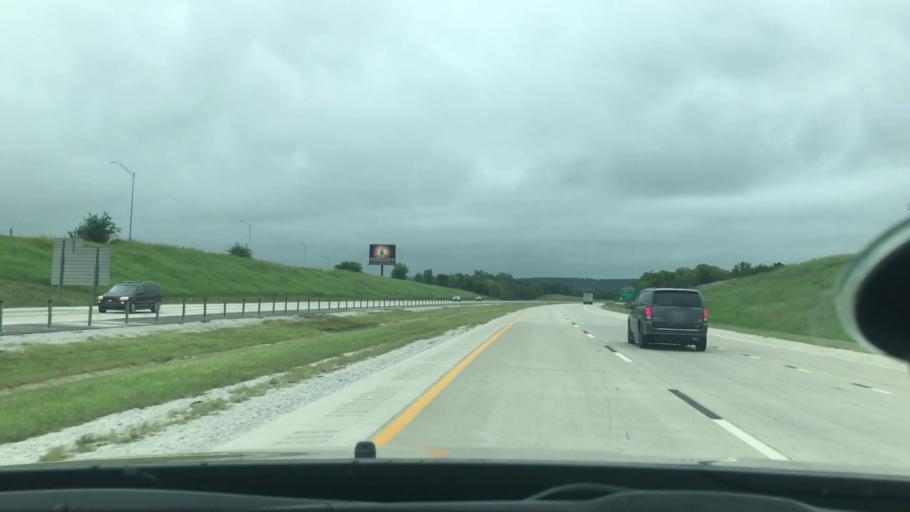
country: US
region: Oklahoma
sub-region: Okmulgee County
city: Henryetta
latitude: 35.4337
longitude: -96.0117
